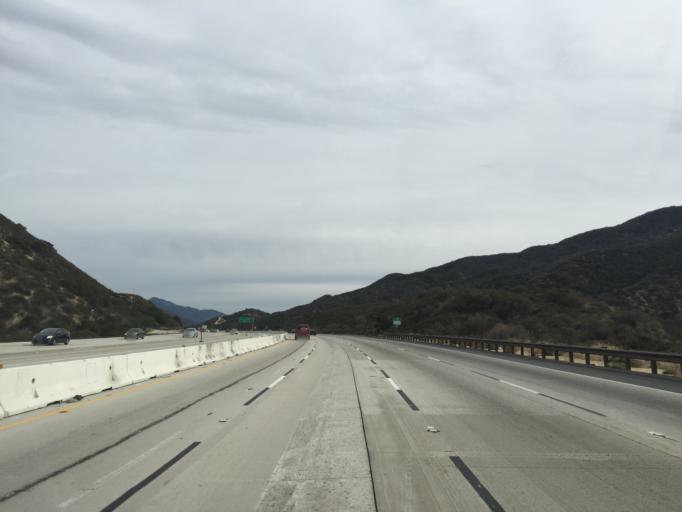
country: US
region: California
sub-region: Los Angeles County
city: Burbank
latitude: 34.2350
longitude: -118.3007
